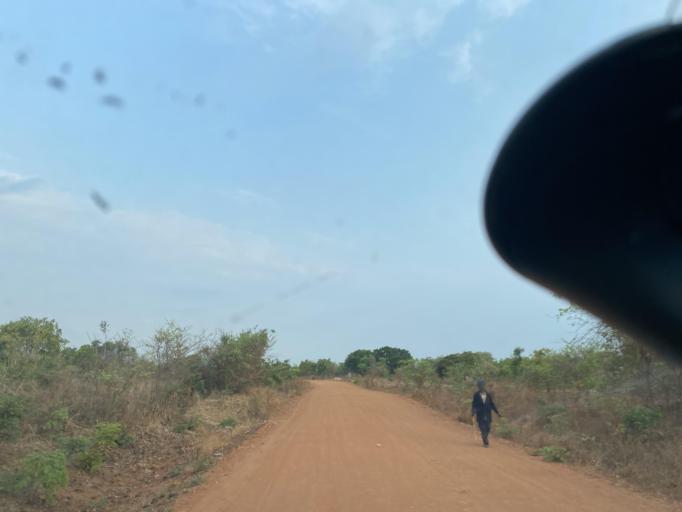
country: ZM
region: Lusaka
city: Chongwe
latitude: -15.2395
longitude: 28.5973
